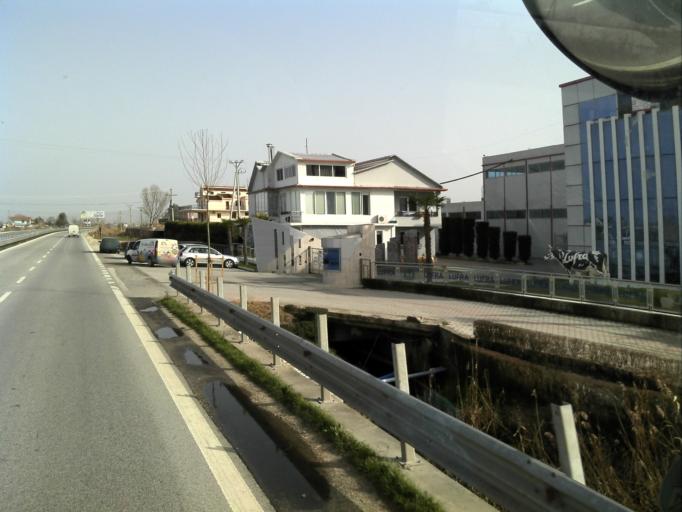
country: AL
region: Fier
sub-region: Rrethi i Lushnjes
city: Krutja e Poshtme
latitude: 40.8660
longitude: 19.6539
